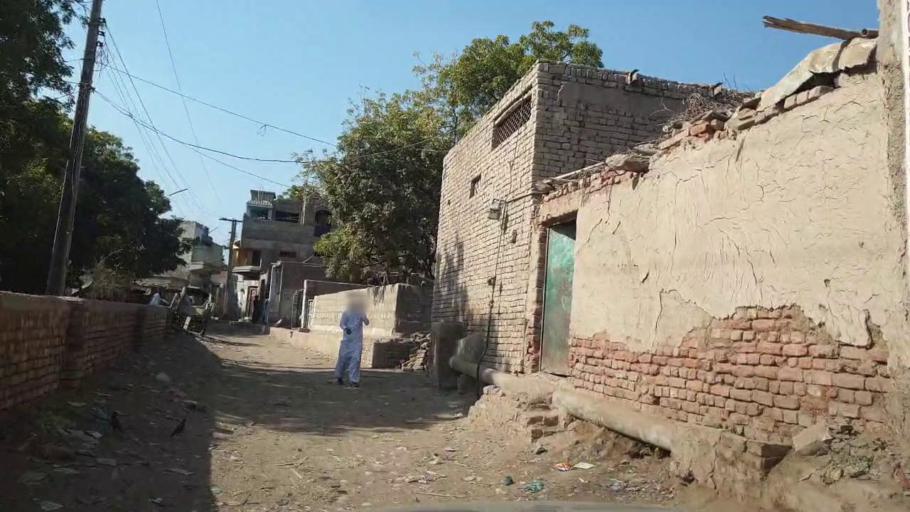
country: PK
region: Sindh
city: Tando Allahyar
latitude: 25.5717
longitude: 68.7143
